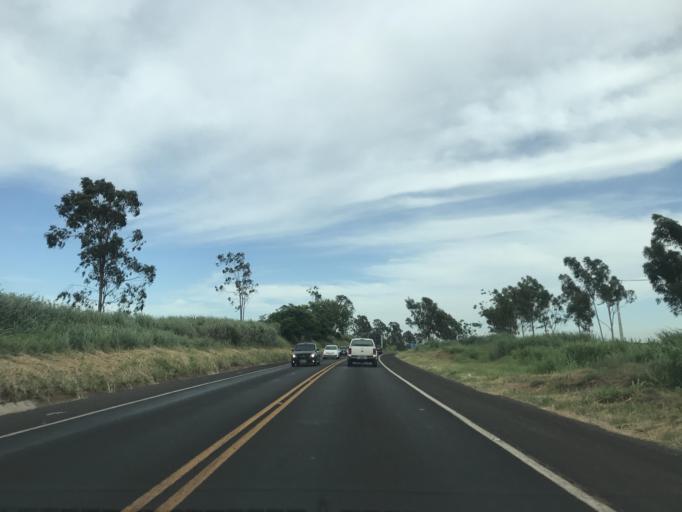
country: BR
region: Parana
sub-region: Paranavai
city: Paranavai
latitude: -23.0147
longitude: -52.5317
